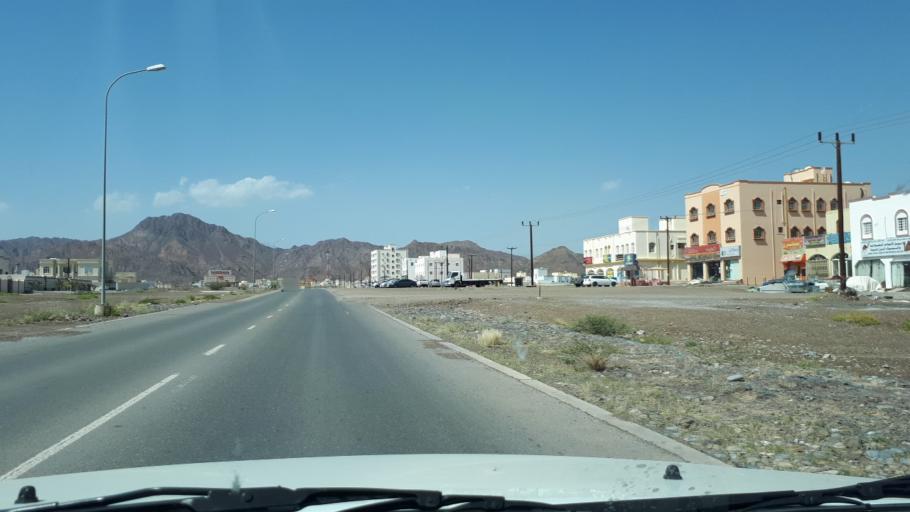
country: OM
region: Muhafazat ad Dakhiliyah
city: Bahla'
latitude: 22.9413
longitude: 57.2591
